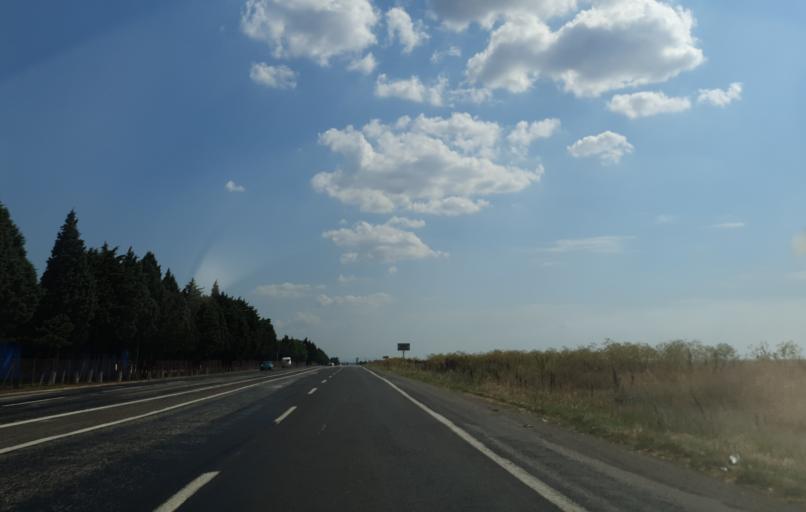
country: TR
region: Kirklareli
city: Buyukkaristiran
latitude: 41.2823
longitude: 27.5575
